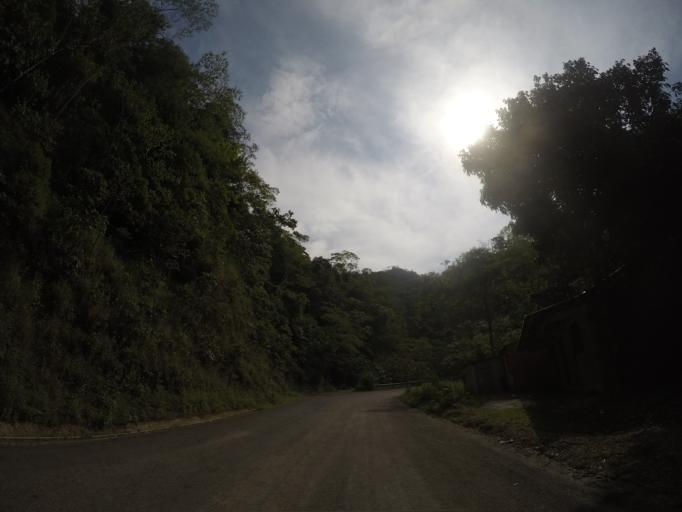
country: MX
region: Oaxaca
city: Pluma Hidalgo
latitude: 15.9338
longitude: -96.4263
